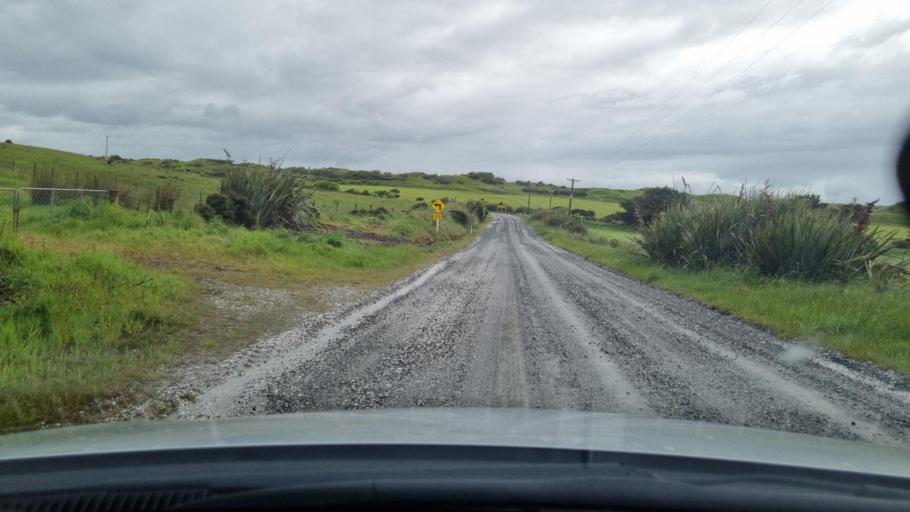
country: NZ
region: Southland
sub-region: Invercargill City
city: Bluff
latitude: -46.5219
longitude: 168.2719
